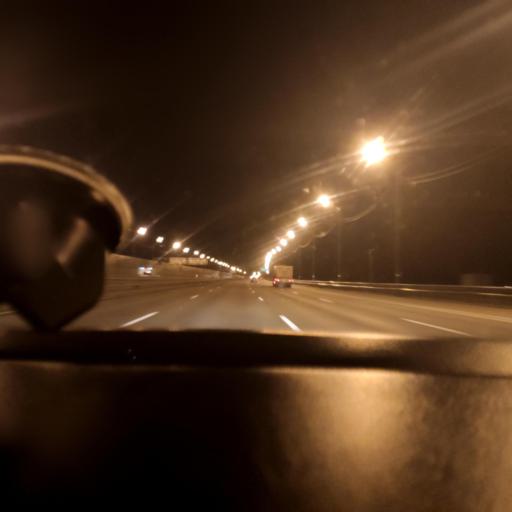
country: RU
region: Moskovskaya
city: Petrovo-Dal'neye
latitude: 55.7830
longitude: 37.1528
